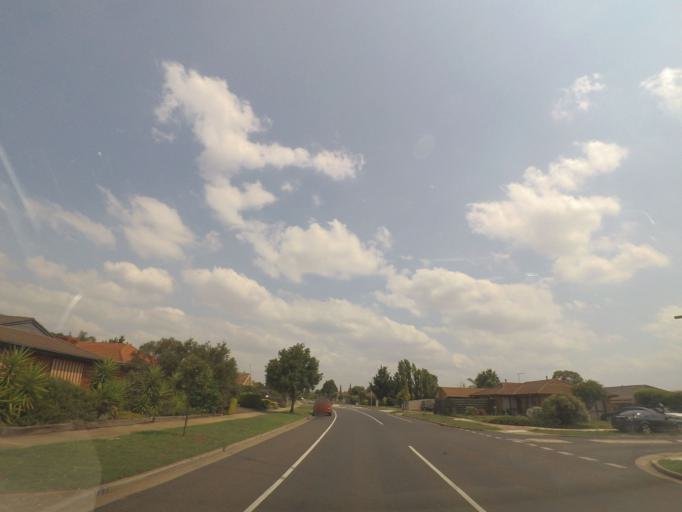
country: AU
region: Victoria
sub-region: Melton
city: Brookfield
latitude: -37.6939
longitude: 144.5611
